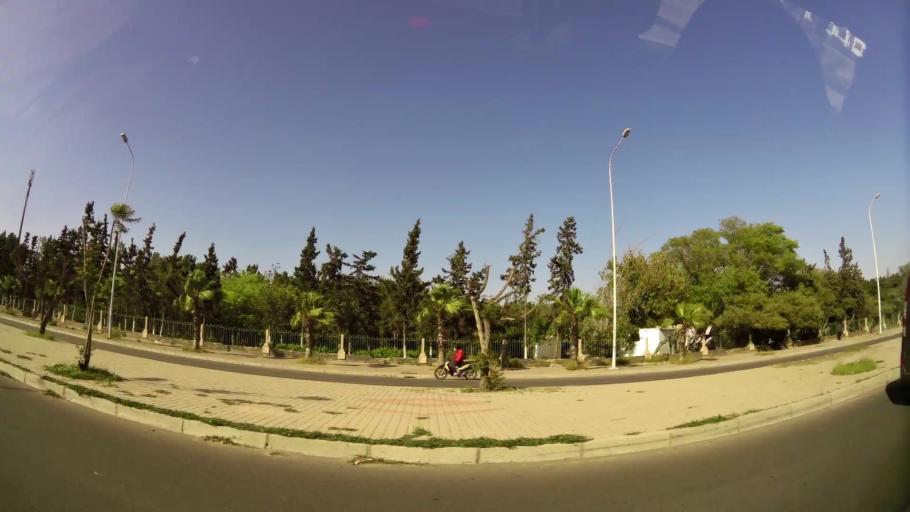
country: MA
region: Oued ed Dahab-Lagouira
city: Dakhla
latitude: 30.4064
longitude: -9.5530
